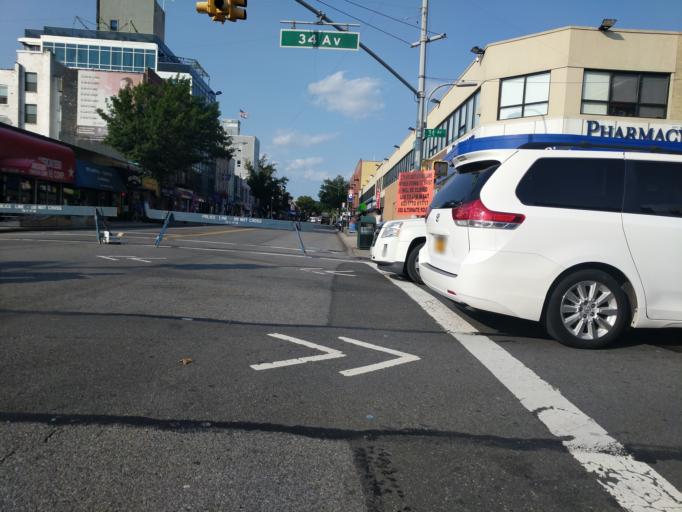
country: US
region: New York
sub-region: Queens County
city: Long Island City
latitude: 40.7566
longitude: -73.9208
